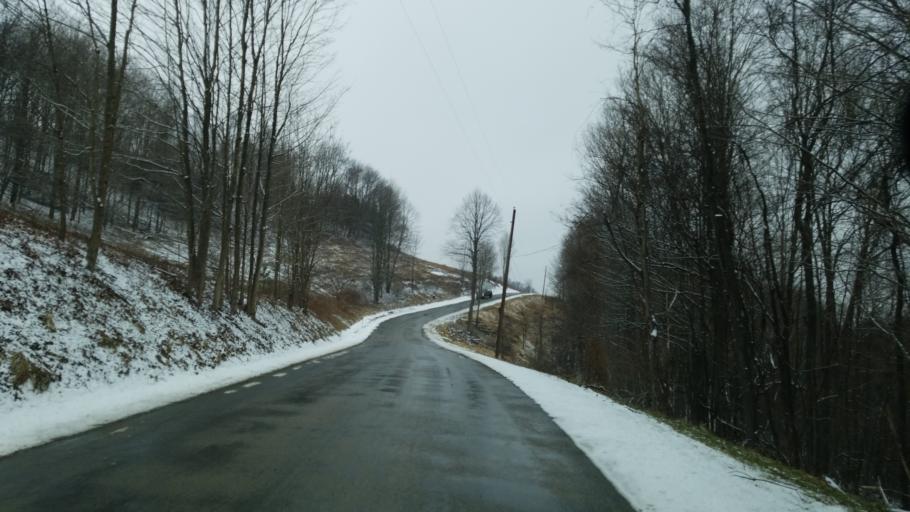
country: US
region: Pennsylvania
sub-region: Jefferson County
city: Sykesville
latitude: 41.0843
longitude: -78.8296
